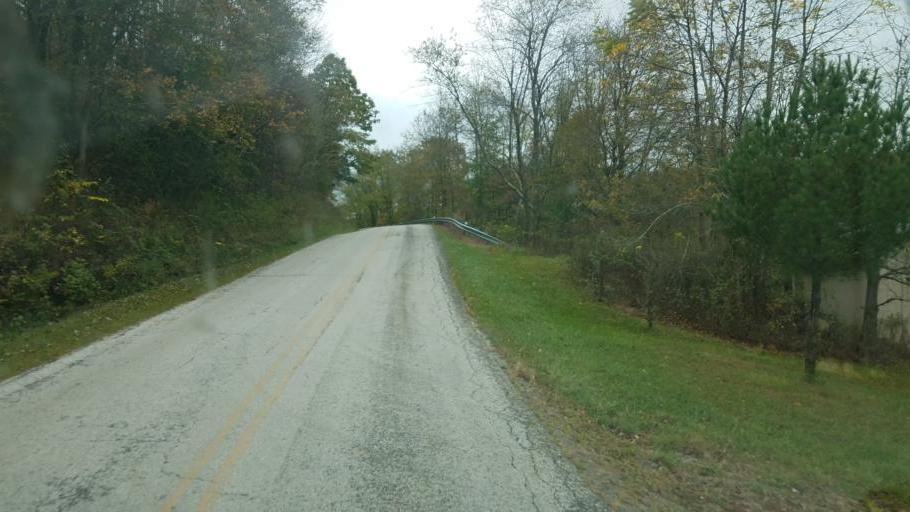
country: US
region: Ohio
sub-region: Ashland County
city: Loudonville
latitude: 40.5529
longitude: -82.1455
